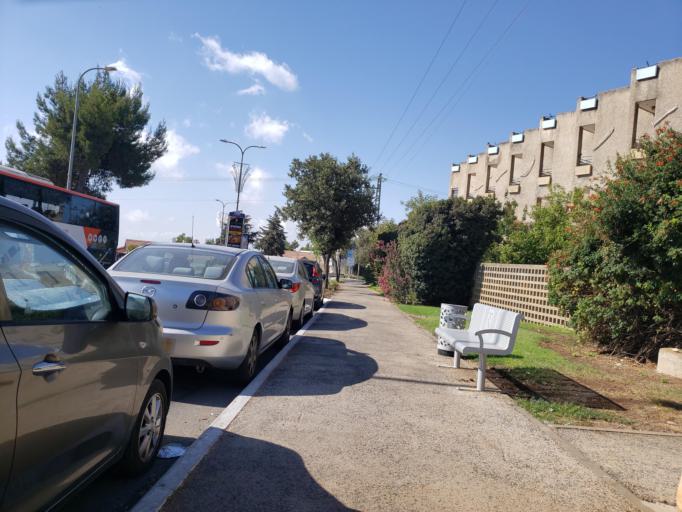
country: IL
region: Northern District
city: Safed
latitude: 32.9641
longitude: 35.4981
